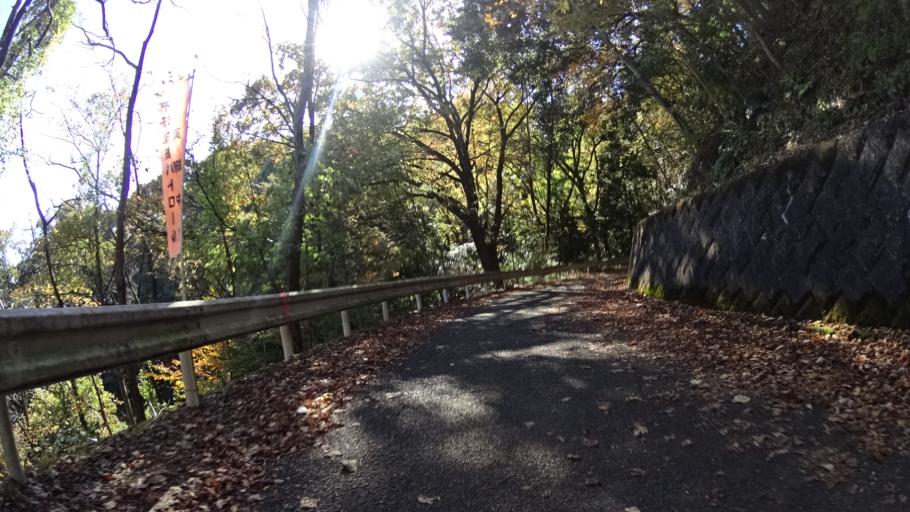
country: JP
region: Kanagawa
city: Zama
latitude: 35.5252
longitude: 139.2735
